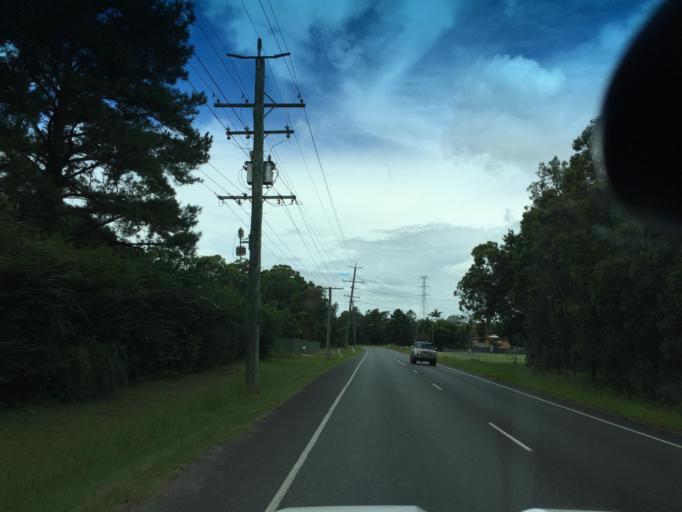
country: AU
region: Queensland
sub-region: Moreton Bay
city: Caboolture
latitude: -27.0666
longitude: 152.9137
